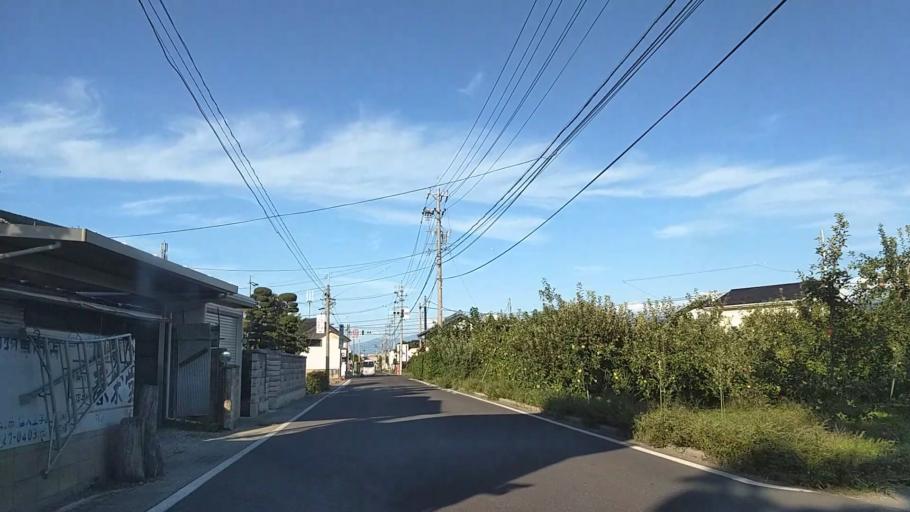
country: JP
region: Nagano
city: Nagano-shi
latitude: 36.6030
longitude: 138.2064
